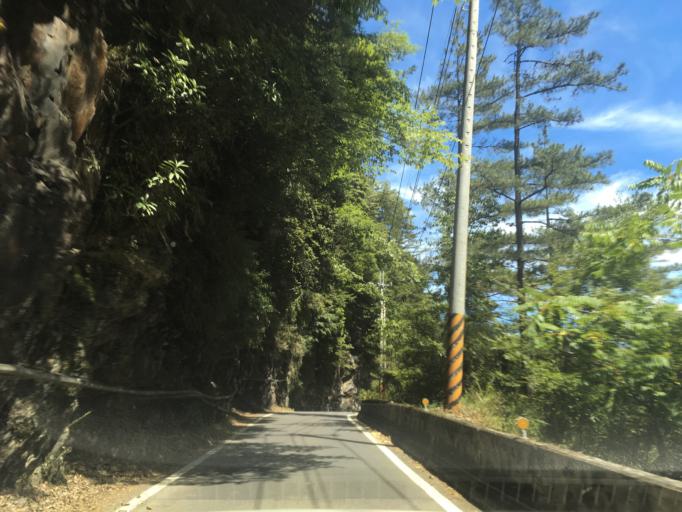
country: TW
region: Taiwan
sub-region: Nantou
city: Puli
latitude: 24.2206
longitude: 121.2644
